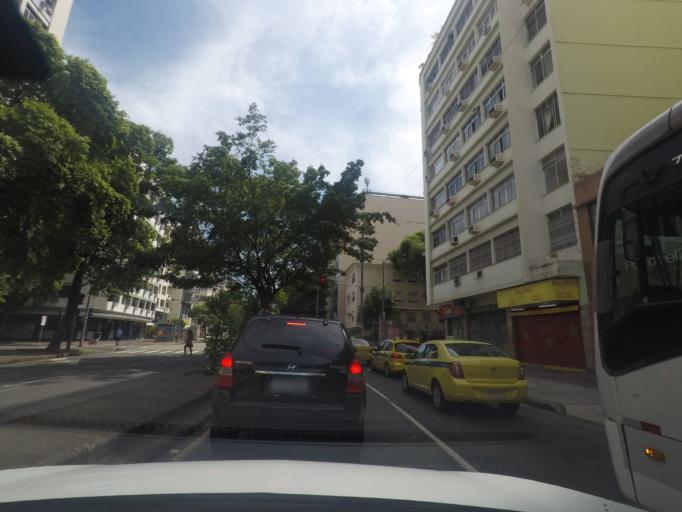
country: BR
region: Rio de Janeiro
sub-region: Rio De Janeiro
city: Rio de Janeiro
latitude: -22.9302
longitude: -43.2376
